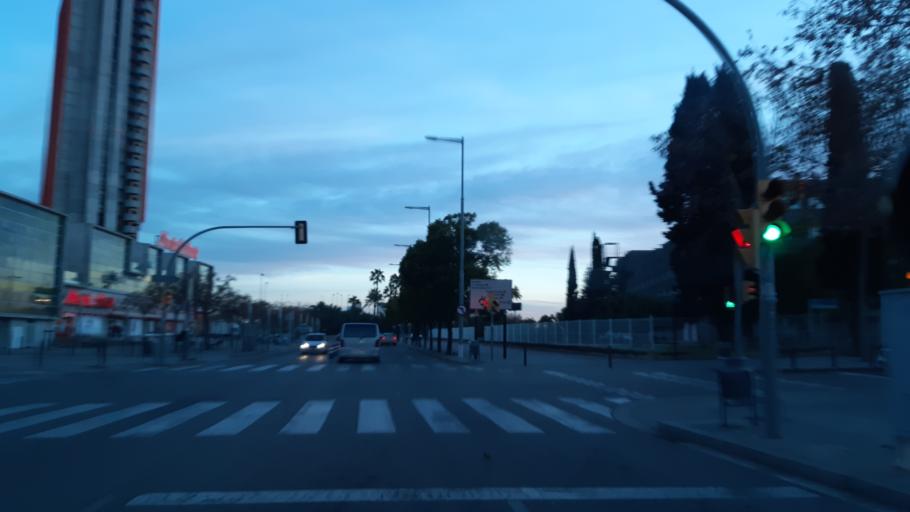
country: ES
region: Catalonia
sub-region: Provincia de Barcelona
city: L'Hospitalet de Llobregat
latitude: 41.3474
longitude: 2.1069
